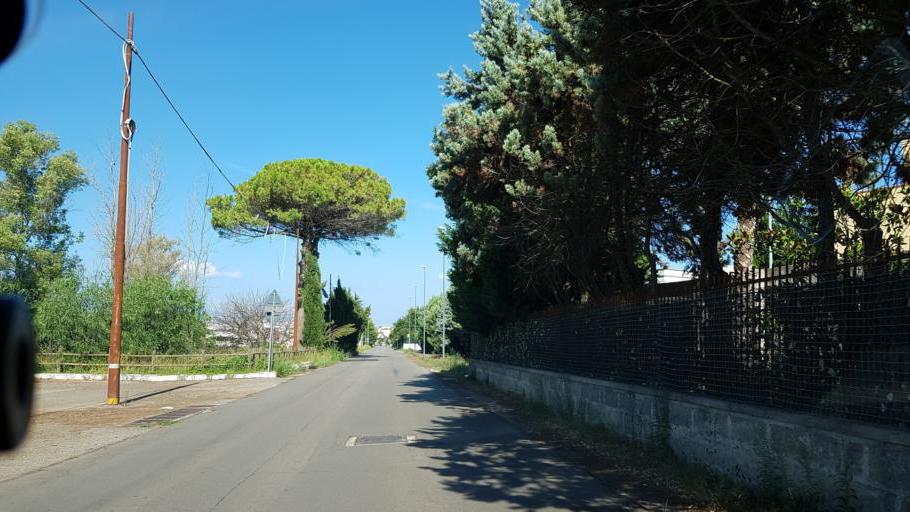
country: IT
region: Apulia
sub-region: Provincia di Lecce
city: San Pietro in Lama
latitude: 40.3038
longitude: 18.1210
